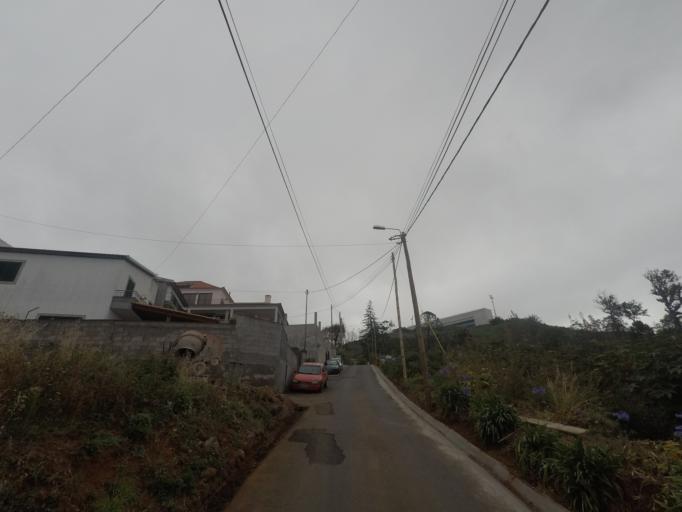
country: PT
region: Madeira
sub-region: Funchal
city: Nossa Senhora do Monte
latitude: 32.6686
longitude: -16.8884
